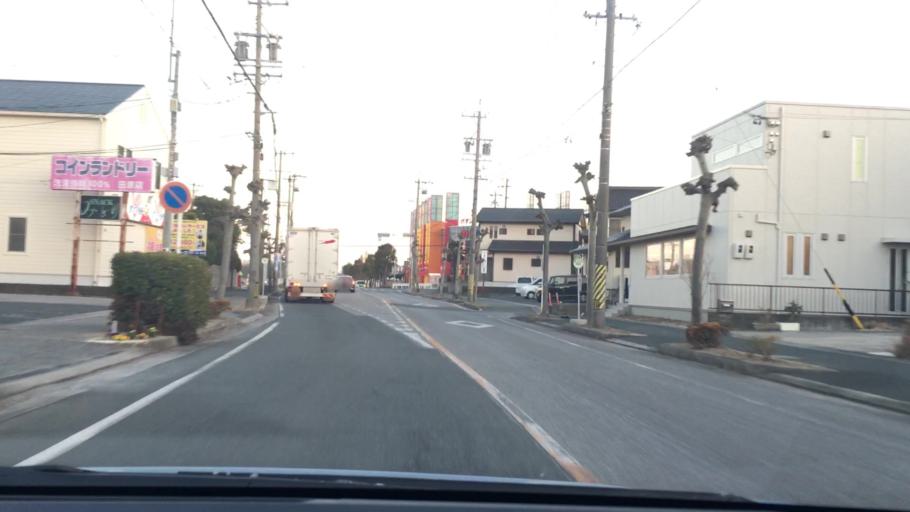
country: JP
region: Aichi
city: Tahara
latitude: 34.6681
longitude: 137.2617
